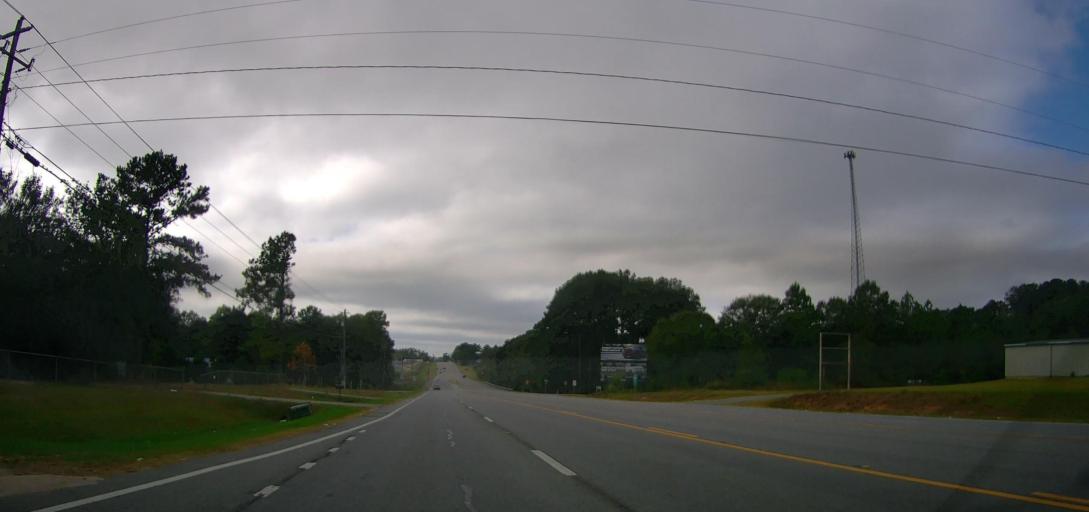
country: US
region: Georgia
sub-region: Colquitt County
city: Moultrie
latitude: 31.2205
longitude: -83.7592
